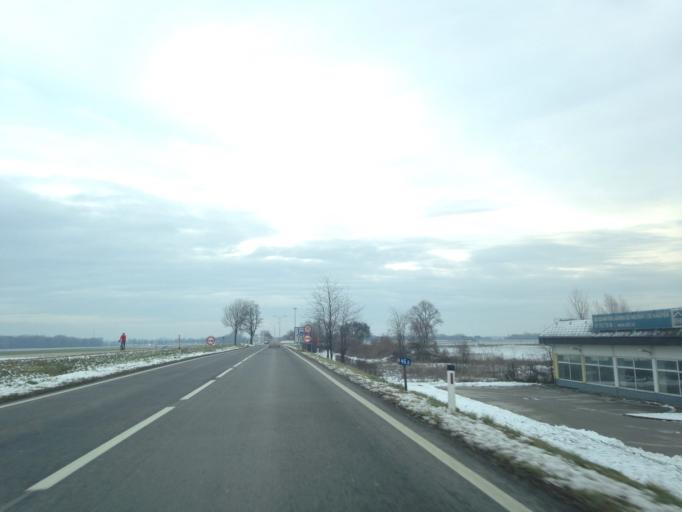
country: AT
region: Lower Austria
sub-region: Politischer Bezirk Bruck an der Leitha
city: Wolfsthal
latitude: 48.1279
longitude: 17.0272
